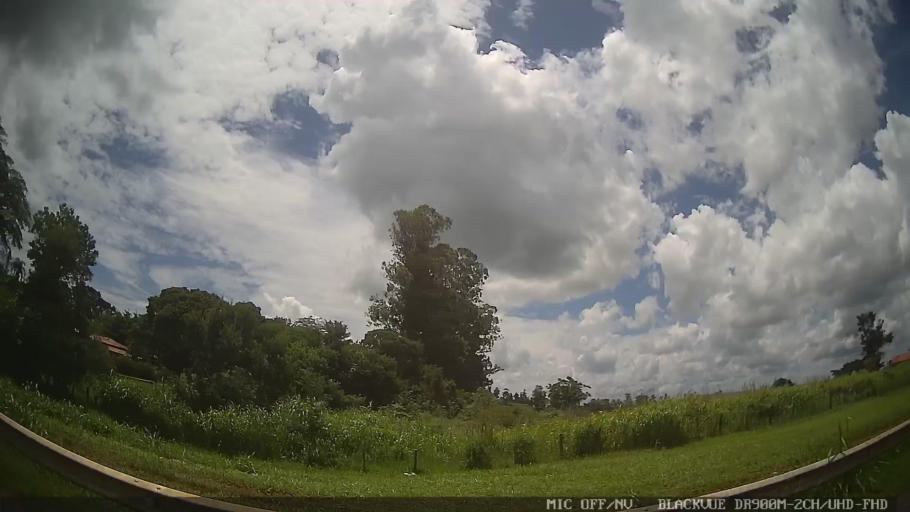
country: BR
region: Sao Paulo
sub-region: Laranjal Paulista
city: Laranjal Paulista
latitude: -23.0407
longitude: -47.9031
